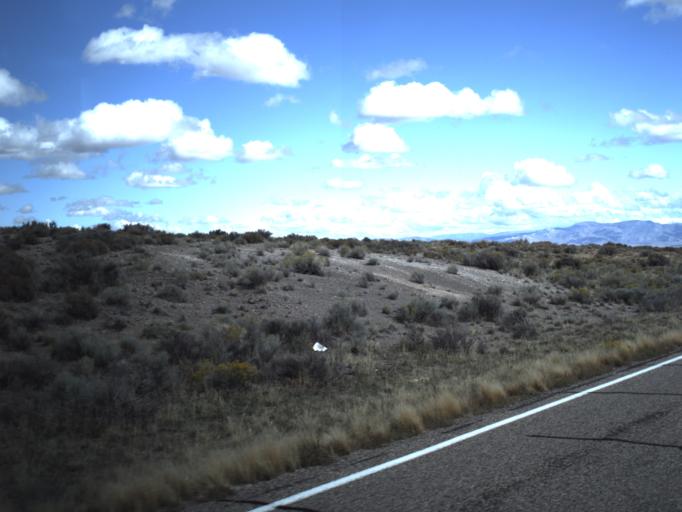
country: US
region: Utah
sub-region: Beaver County
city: Milford
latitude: 38.4513
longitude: -113.2011
